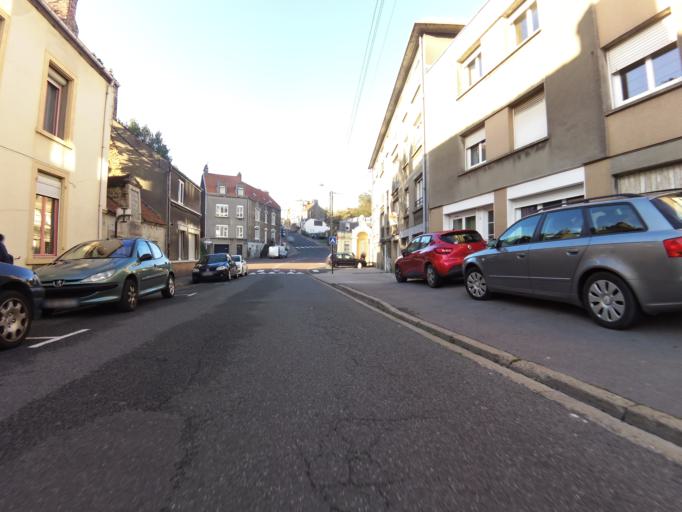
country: FR
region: Nord-Pas-de-Calais
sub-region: Departement du Pas-de-Calais
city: Saint-Martin-Boulogne
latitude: 50.7334
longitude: 1.6144
